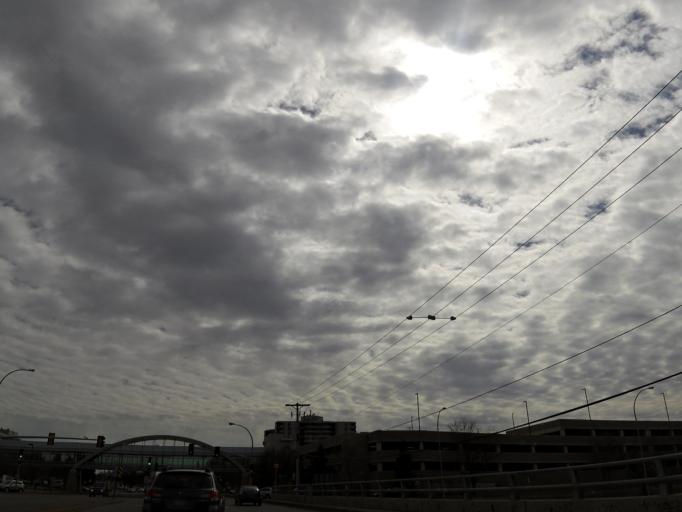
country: US
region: Minnesota
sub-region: Hennepin County
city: Edina
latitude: 44.8873
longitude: -93.3290
